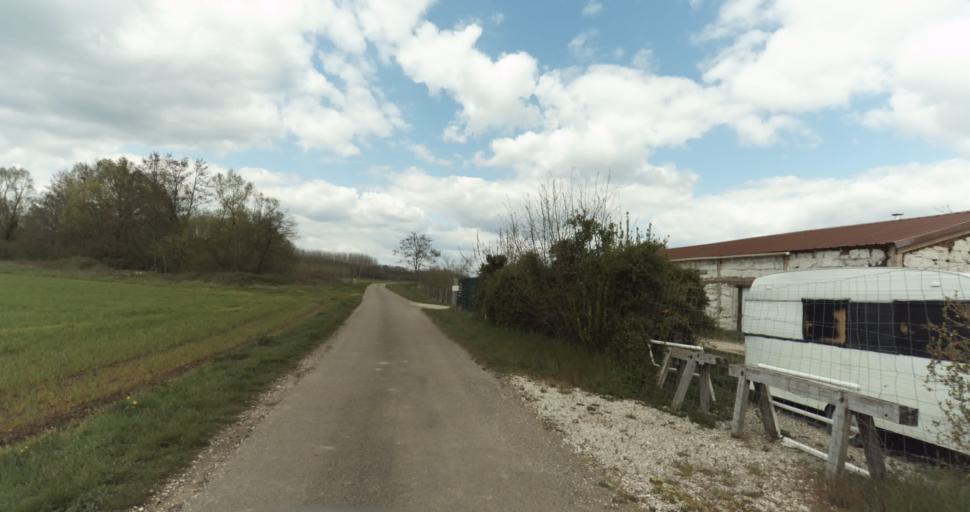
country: FR
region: Bourgogne
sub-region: Departement de la Cote-d'Or
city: Auxonne
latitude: 47.1663
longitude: 5.3950
